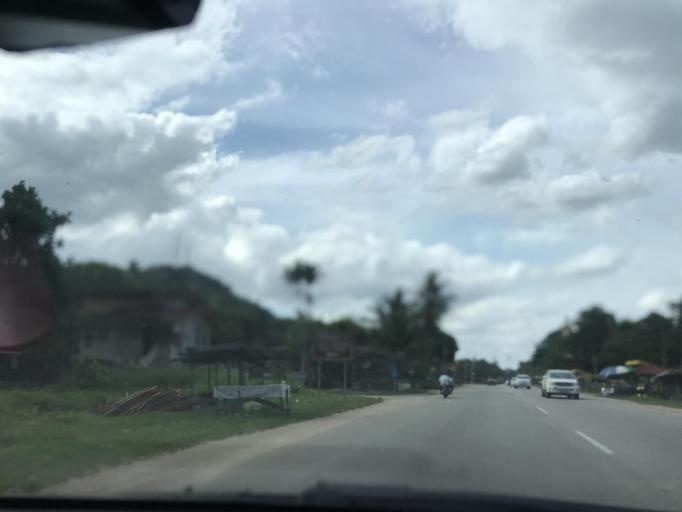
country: MY
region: Kelantan
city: Kampong Pangkal Kalong
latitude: 5.8826
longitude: 102.1770
